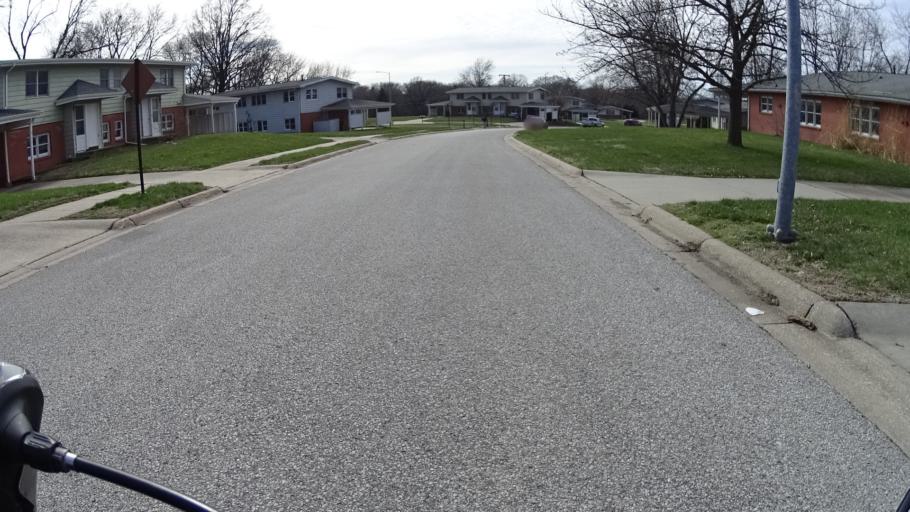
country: US
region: Nebraska
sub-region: Sarpy County
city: Offutt Air Force Base
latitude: 41.1186
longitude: -95.9641
